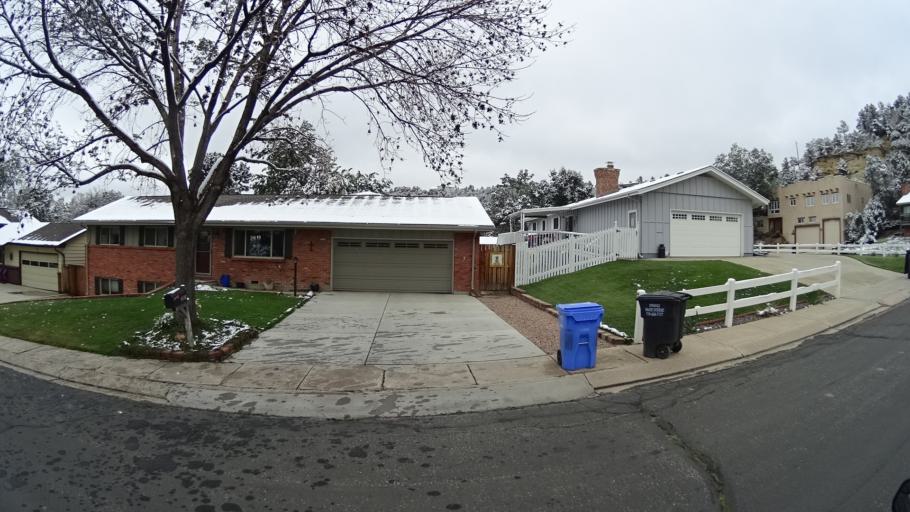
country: US
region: Colorado
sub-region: El Paso County
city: Colorado Springs
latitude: 38.8916
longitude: -104.7773
